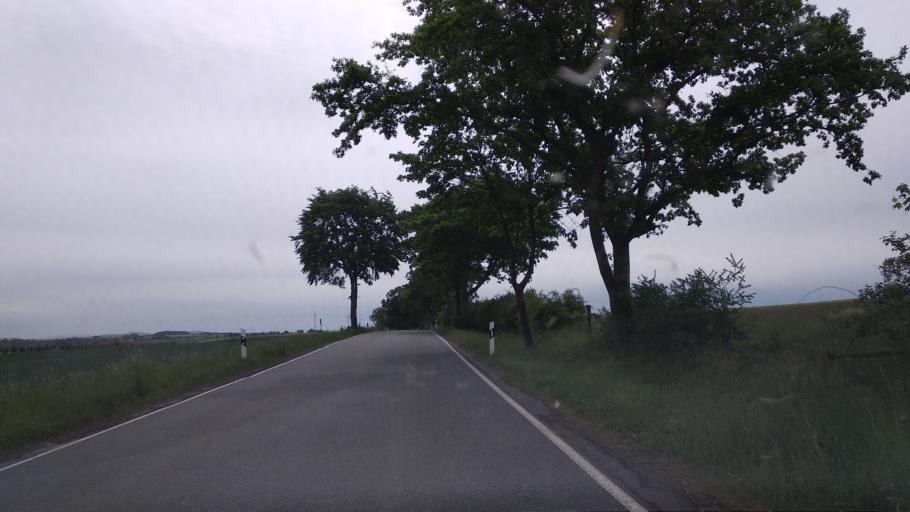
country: DE
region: North Rhine-Westphalia
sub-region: Regierungsbezirk Detmold
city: Willebadessen
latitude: 51.6098
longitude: 9.1123
